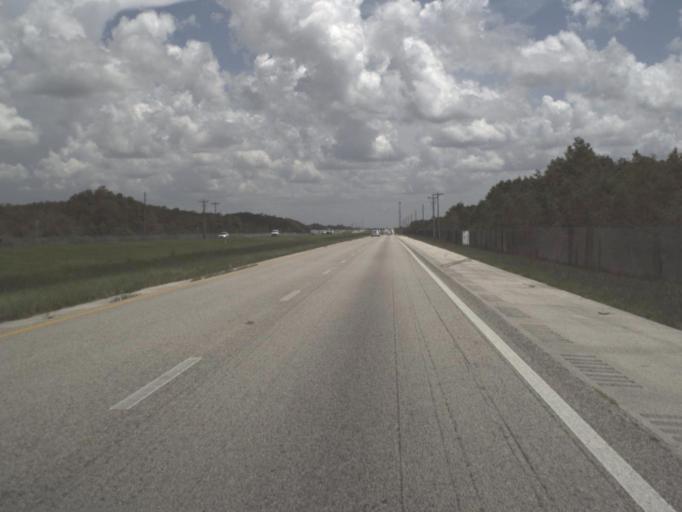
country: US
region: Florida
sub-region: Broward County
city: Weston
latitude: 26.1719
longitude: -80.9095
